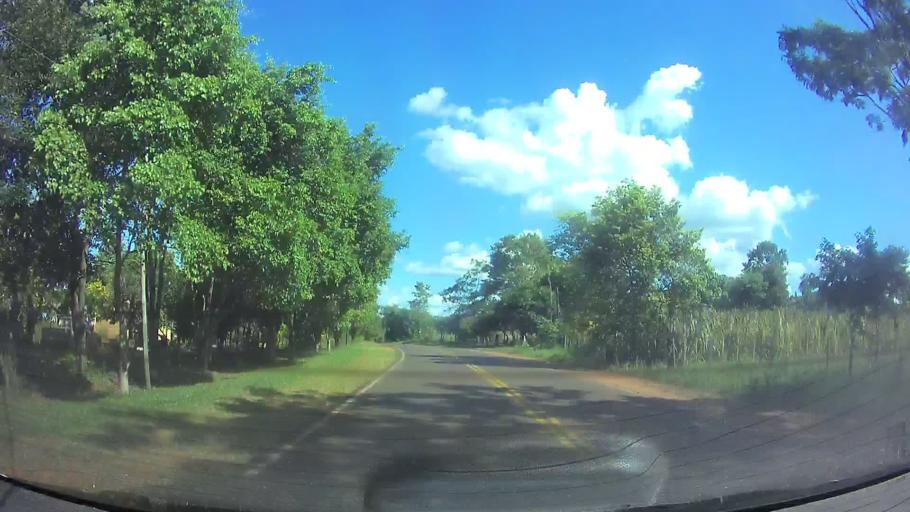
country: PY
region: Paraguari
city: Sapucai
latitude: -25.6553
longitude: -56.8608
